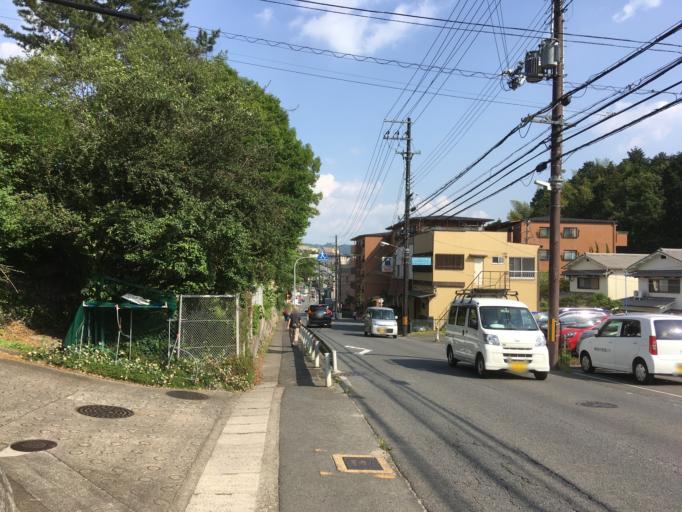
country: JP
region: Nara
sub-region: Ikoma-shi
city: Ikoma
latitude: 34.6882
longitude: 135.6998
